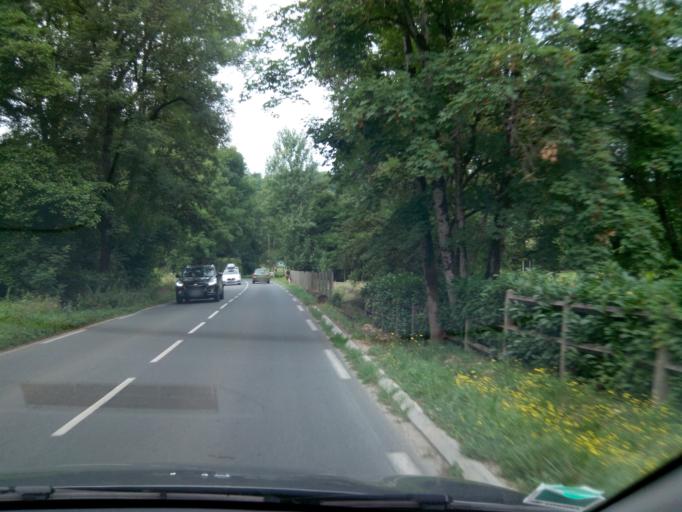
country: FR
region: Aquitaine
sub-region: Departement de la Dordogne
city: Eyvigues-et-Eybenes
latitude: 44.8874
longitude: 1.3844
